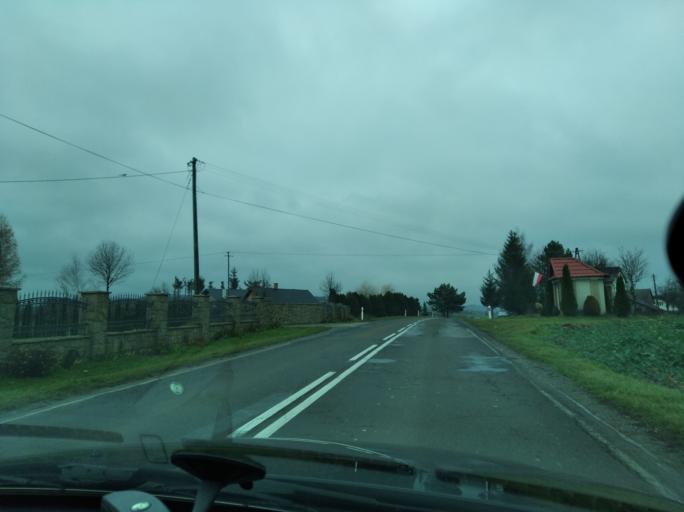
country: PL
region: Subcarpathian Voivodeship
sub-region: Powiat rzeszowski
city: Dynow
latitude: 49.8449
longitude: 22.2436
